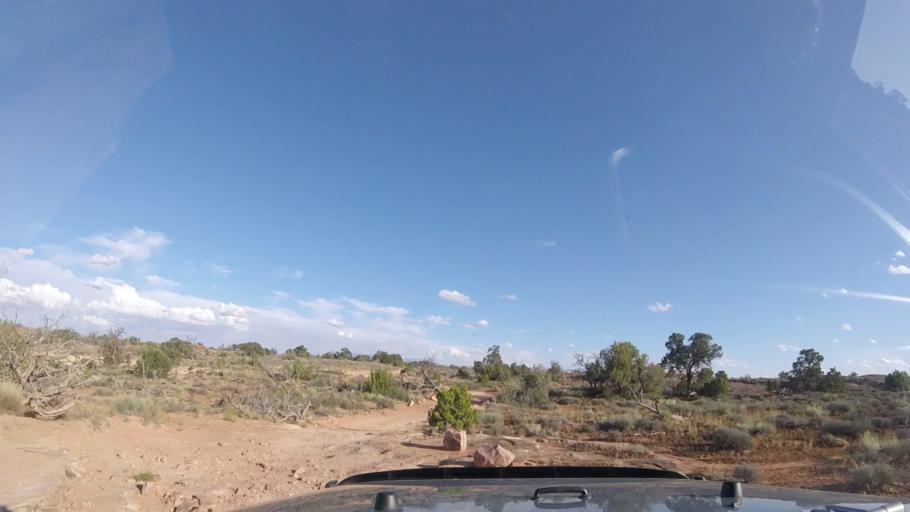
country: US
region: Utah
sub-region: Grand County
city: Moab
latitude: 38.2150
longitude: -109.8122
